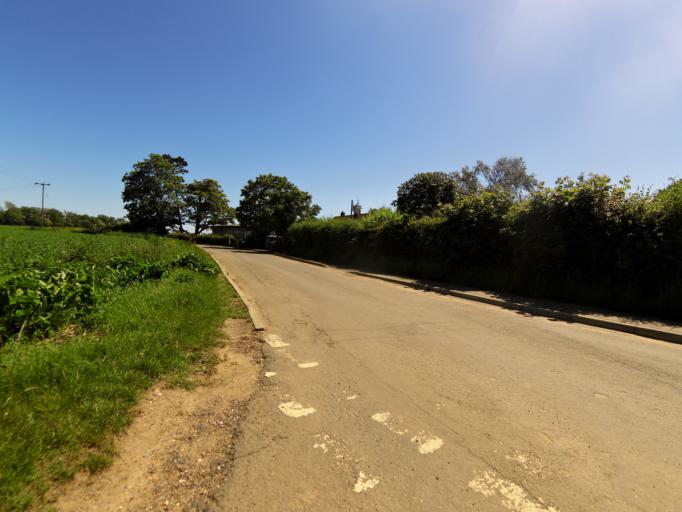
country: GB
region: England
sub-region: Suffolk
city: Felixstowe
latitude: 52.0086
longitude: 1.4218
